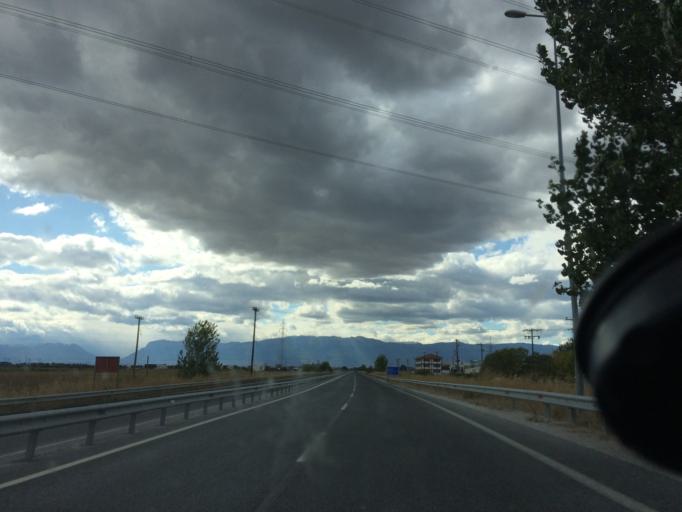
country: GR
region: Thessaly
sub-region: Trikala
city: Taxiarches
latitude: 39.5630
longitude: 21.8816
